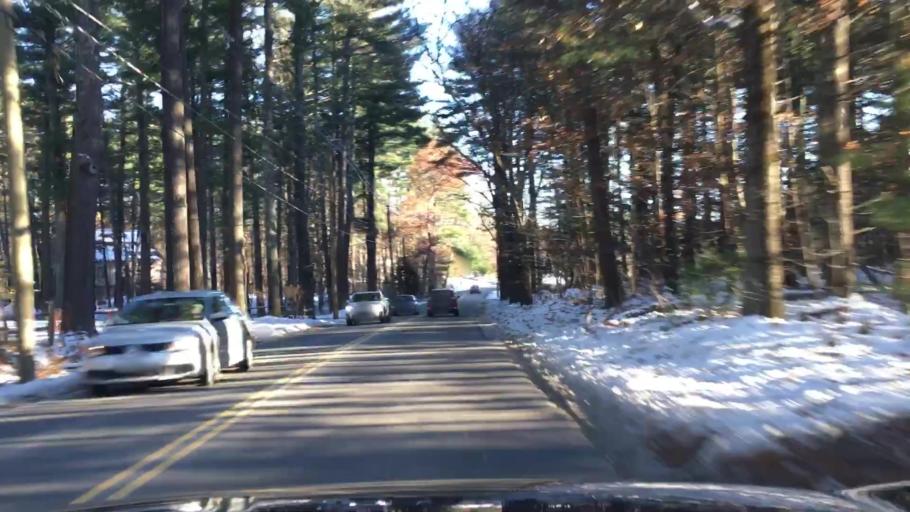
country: US
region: New Hampshire
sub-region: Hillsborough County
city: Hollis
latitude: 42.8102
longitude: -71.5610
